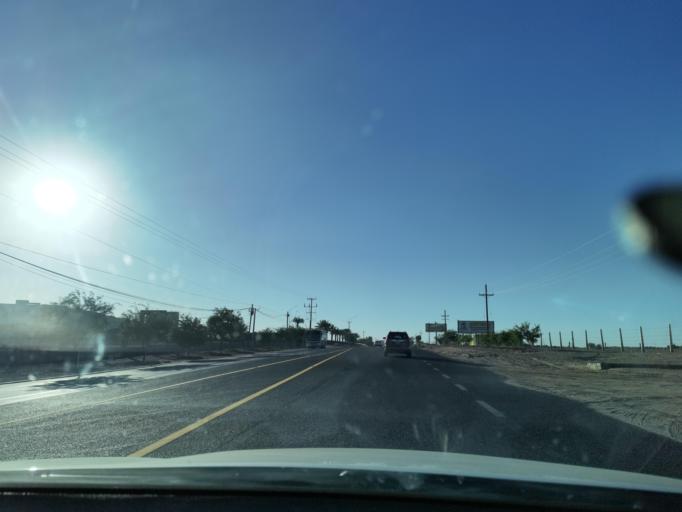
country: MX
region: Baja California
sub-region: Mexicali
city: Islas Agrarias Grupo A
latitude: 32.6350
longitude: -115.2773
